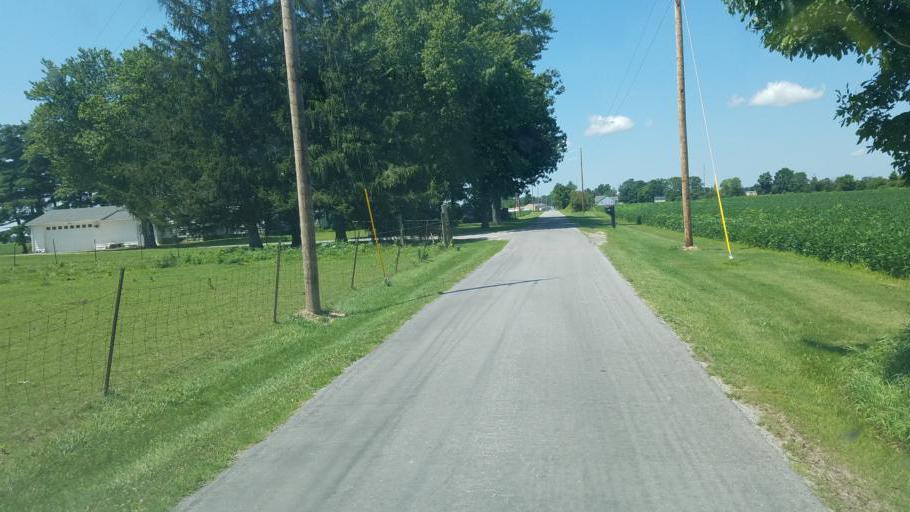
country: US
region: Ohio
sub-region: Marion County
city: Prospect
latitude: 40.5141
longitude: -83.2228
